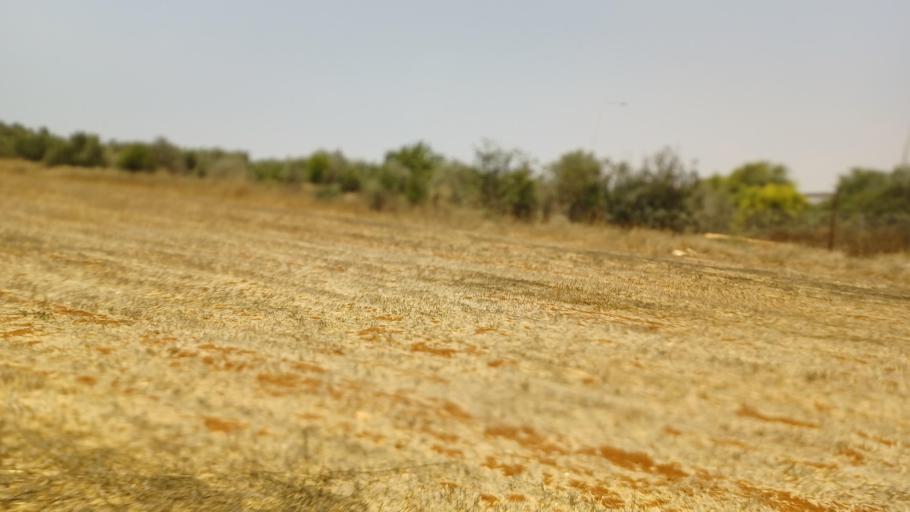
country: CY
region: Ammochostos
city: Liopetri
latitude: 34.9669
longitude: 33.8648
